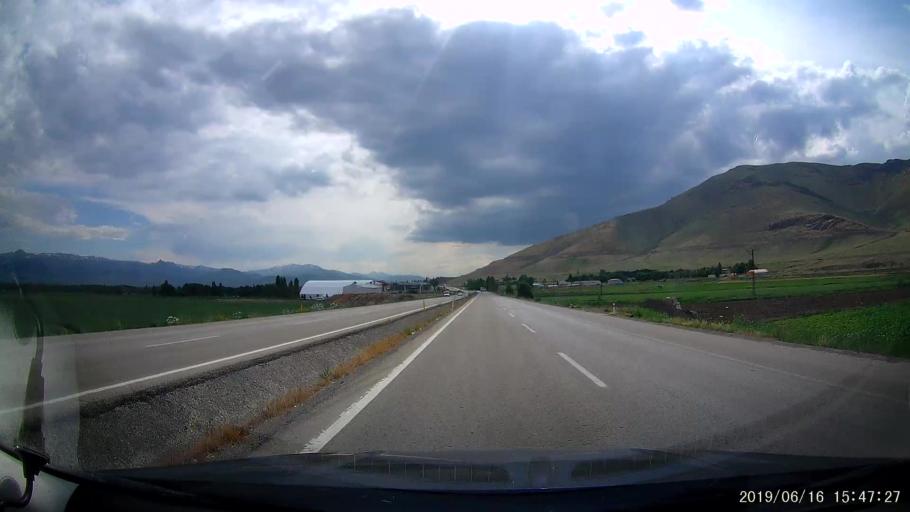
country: TR
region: Erzurum
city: Pasinler
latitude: 39.9884
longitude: 41.7206
